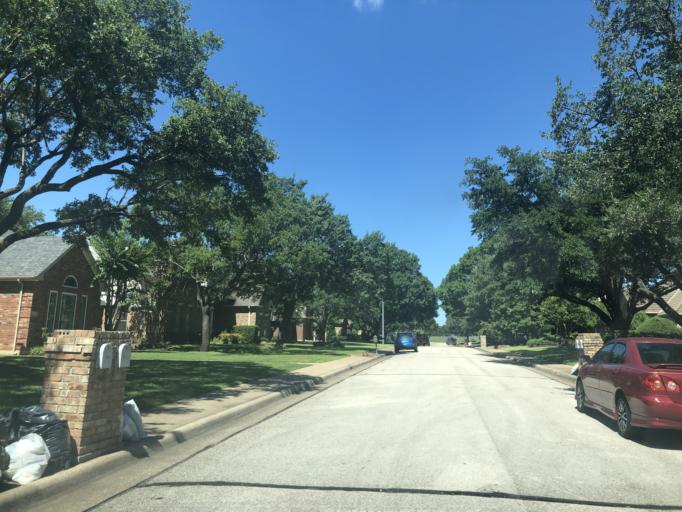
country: US
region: Texas
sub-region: Dallas County
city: Duncanville
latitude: 32.6449
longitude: -96.9282
